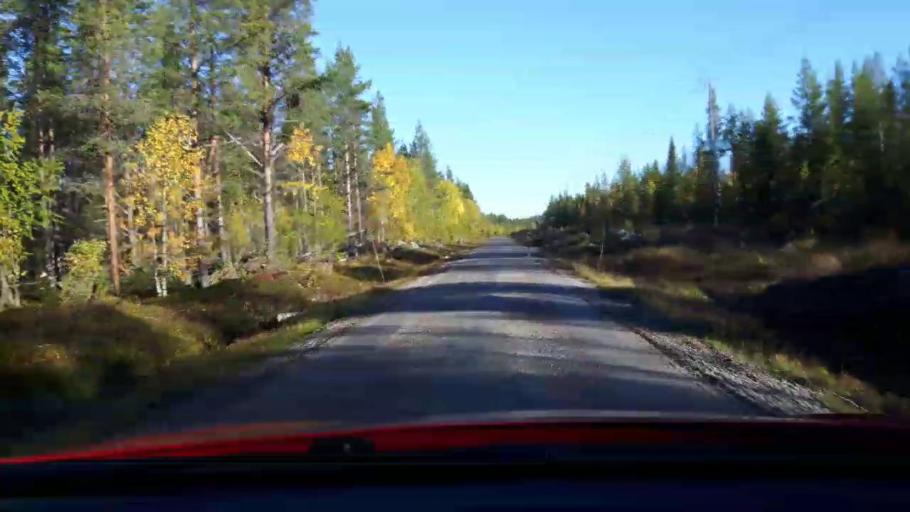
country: SE
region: Jaemtland
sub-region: Stroemsunds Kommun
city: Stroemsund
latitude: 64.3874
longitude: 15.1516
